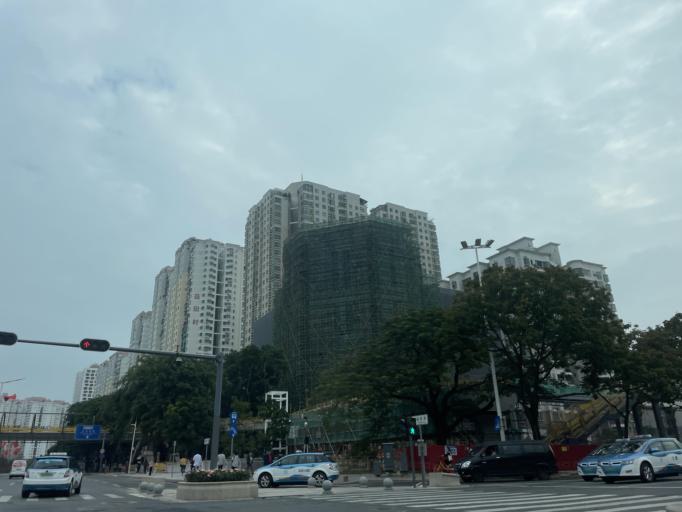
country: CN
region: Guangdong
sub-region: Shenzhen
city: Shenzhen
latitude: 22.5211
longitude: 114.0418
